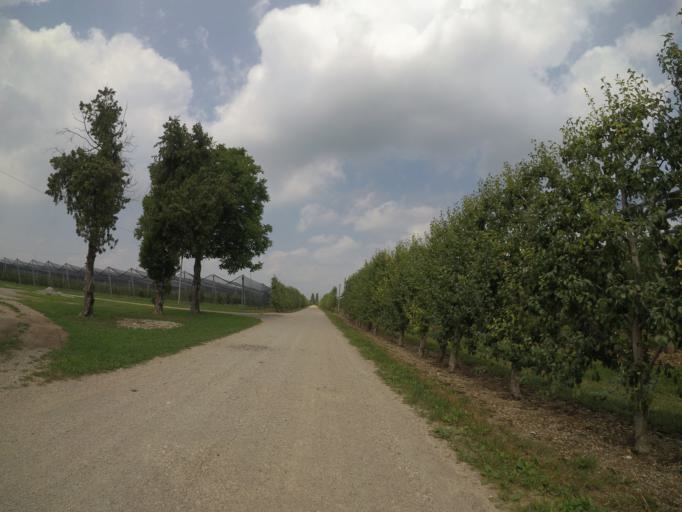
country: IT
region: Friuli Venezia Giulia
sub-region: Provincia di Udine
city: Sedegliano
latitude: 45.9931
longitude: 13.0108
